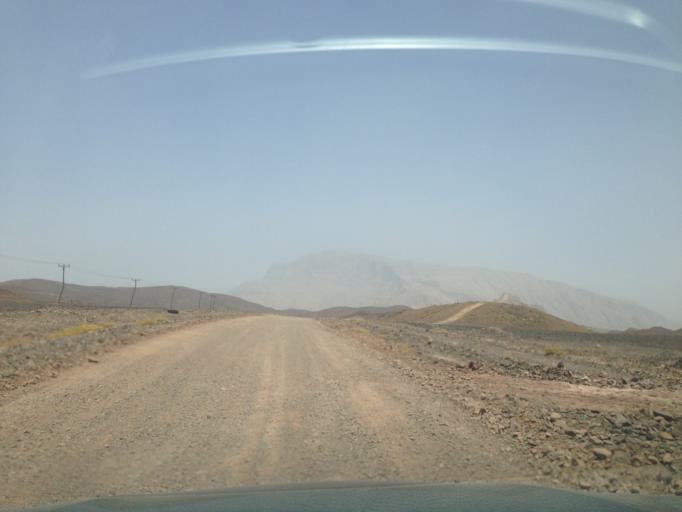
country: OM
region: Az Zahirah
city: `Ibri
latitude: 23.2039
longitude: 56.8574
